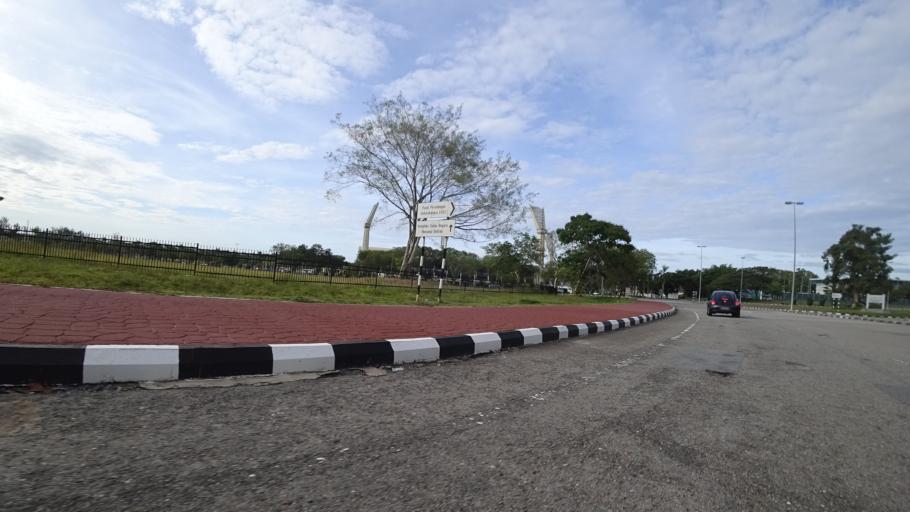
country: BN
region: Brunei and Muara
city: Bandar Seri Begawan
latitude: 4.9259
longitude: 114.9462
